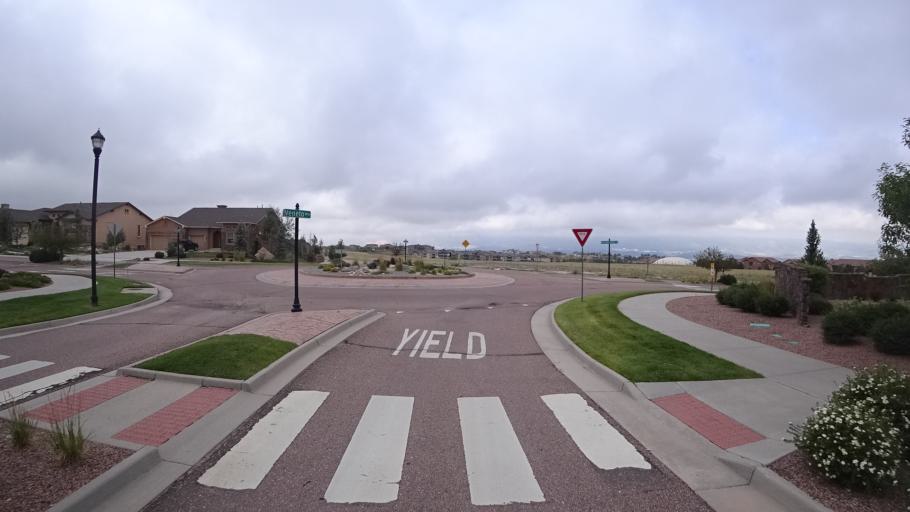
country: US
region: Colorado
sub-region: El Paso County
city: Gleneagle
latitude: 39.0184
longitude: -104.7828
